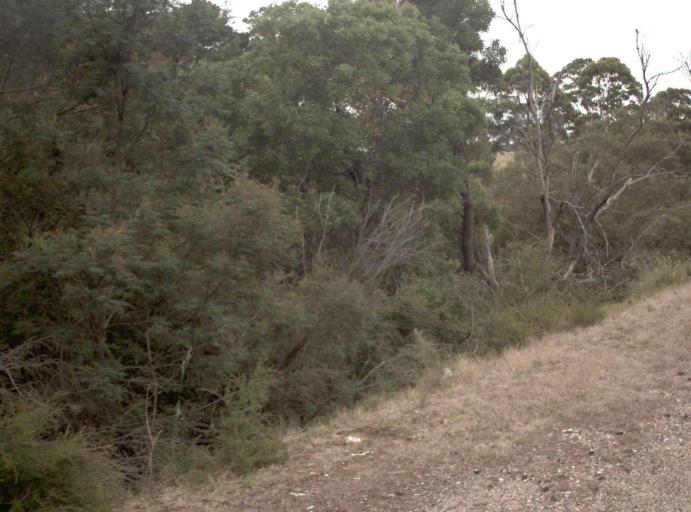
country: AU
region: Victoria
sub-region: Wellington
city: Sale
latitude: -38.1726
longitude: 147.1704
